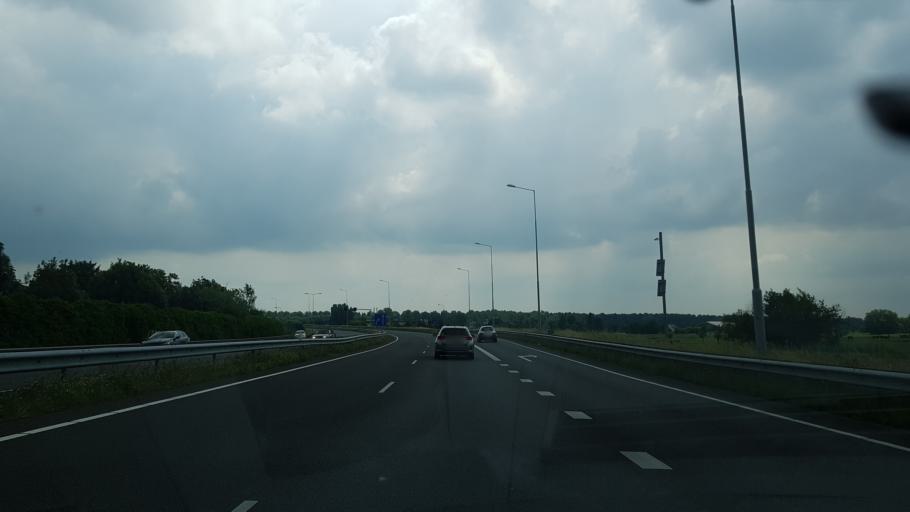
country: NL
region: South Holland
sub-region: Bodegraven-Reeuwijk
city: Bodegraven
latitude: 52.0741
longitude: 4.7392
